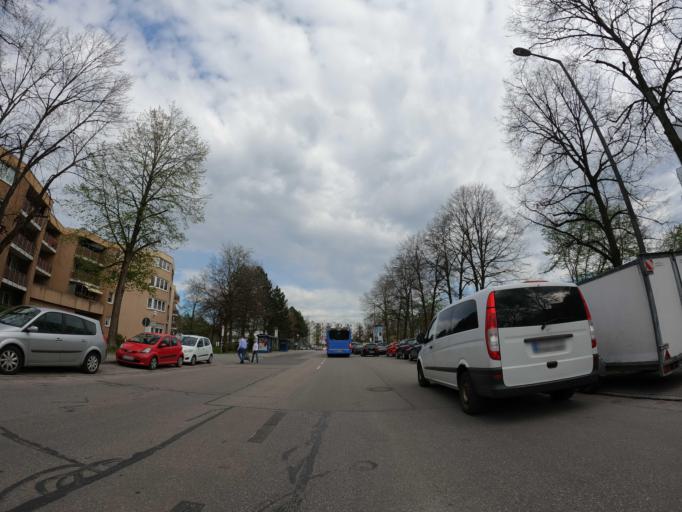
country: DE
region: Bavaria
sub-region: Upper Bavaria
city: Neubiberg
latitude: 48.0967
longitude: 11.6543
